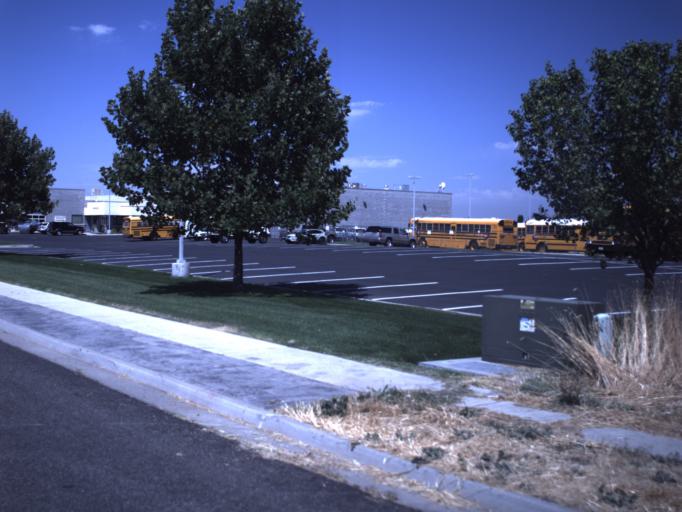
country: US
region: Utah
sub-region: Weber County
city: Marriott-Slaterville
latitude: 41.2287
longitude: -112.0279
